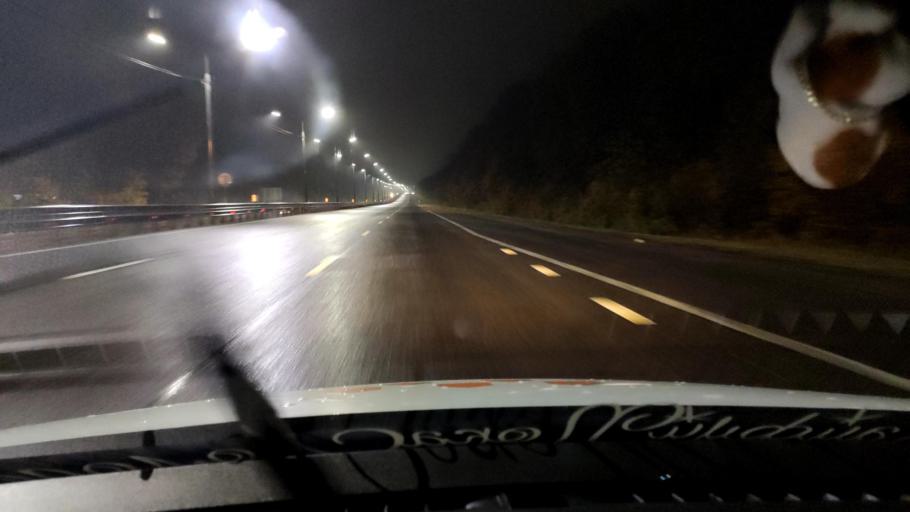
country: RU
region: Voronezj
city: Podgornoye
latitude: 51.8085
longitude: 39.2055
